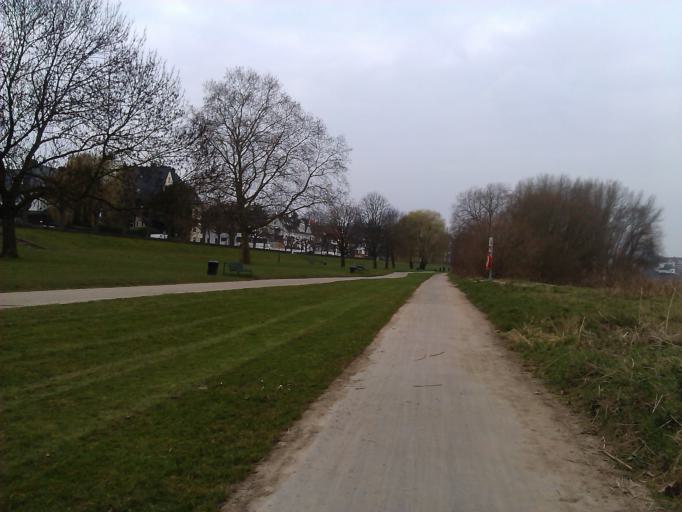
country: DE
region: North Rhine-Westphalia
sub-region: Regierungsbezirk Koln
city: Poll
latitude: 50.8926
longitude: 7.0064
